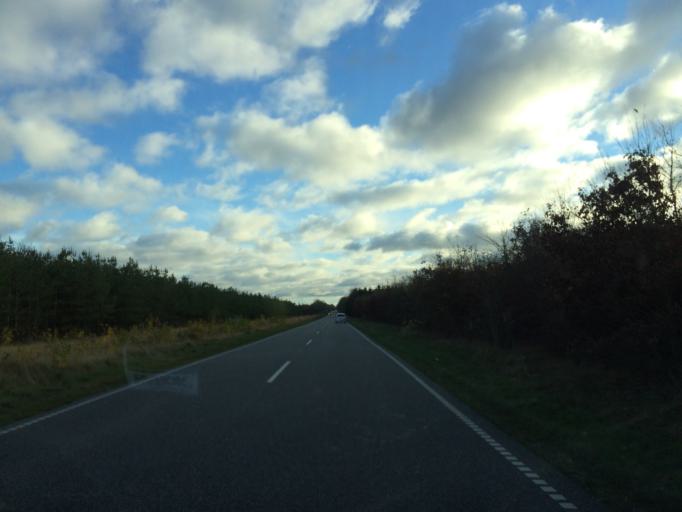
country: DK
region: Central Jutland
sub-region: Herning Kommune
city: Kibaek
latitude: 55.9430
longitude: 8.8882
